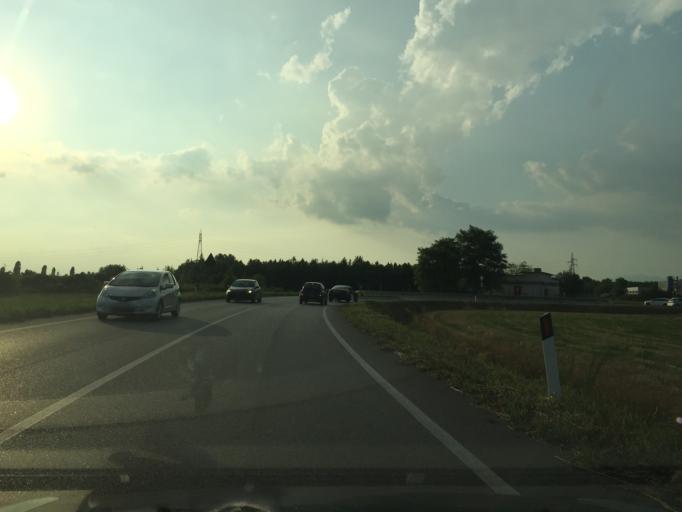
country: IT
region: Friuli Venezia Giulia
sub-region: Provincia di Udine
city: Manzano
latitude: 45.9781
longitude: 13.3548
